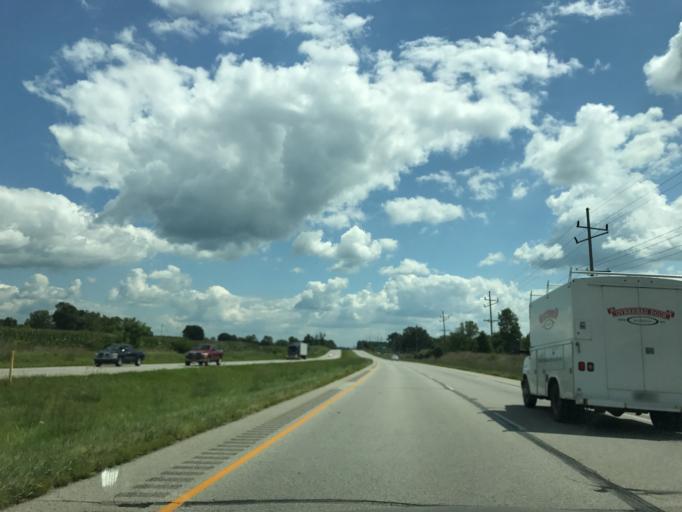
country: US
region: Indiana
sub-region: Kosciusko County
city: Pierceton
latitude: 41.2104
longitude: -85.7408
